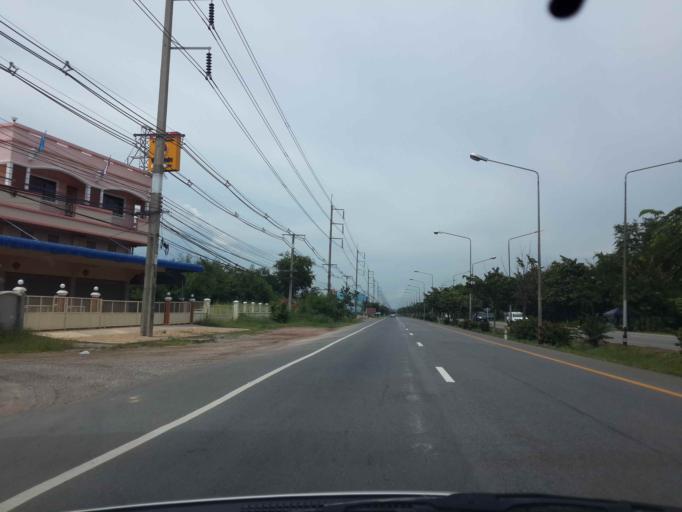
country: TH
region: Ratchaburi
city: Pak Tho
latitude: 13.3523
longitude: 99.8275
